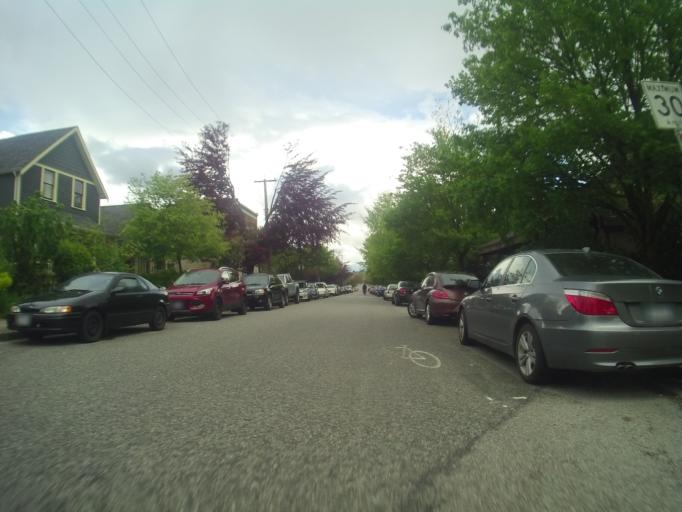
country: CA
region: British Columbia
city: Vancouver
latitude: 49.2774
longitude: -123.0871
